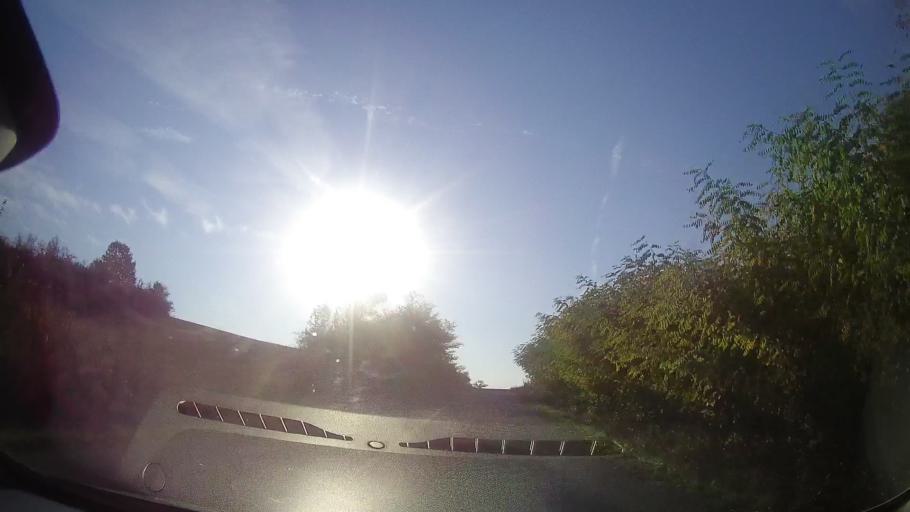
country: RO
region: Timis
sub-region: Comuna Bogda
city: Bogda
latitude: 45.9680
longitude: 21.6072
